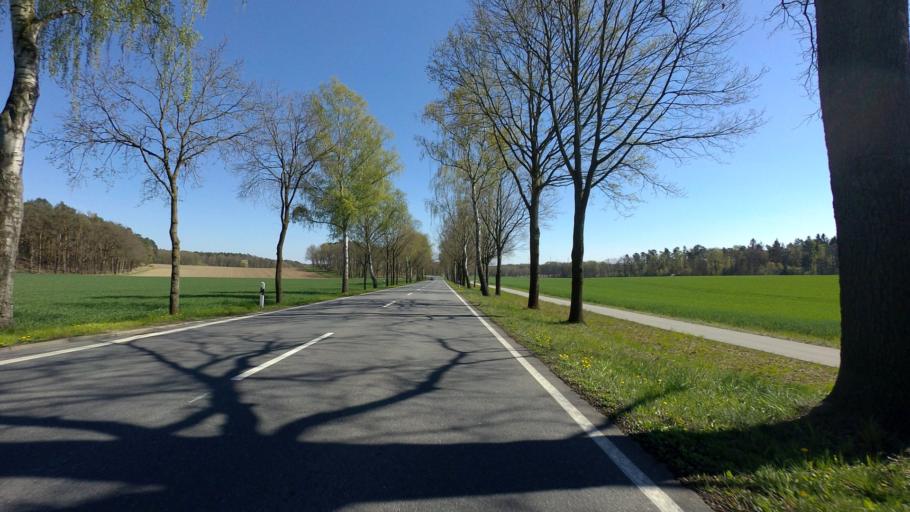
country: DE
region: Lower Saxony
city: Schnega
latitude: 52.9110
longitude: 10.8978
